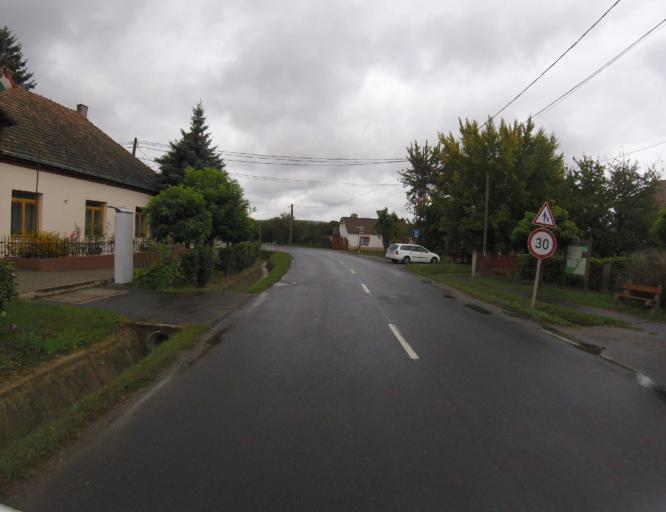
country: HU
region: Komarom-Esztergom
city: Esztergom
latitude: 47.8860
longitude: 18.7762
